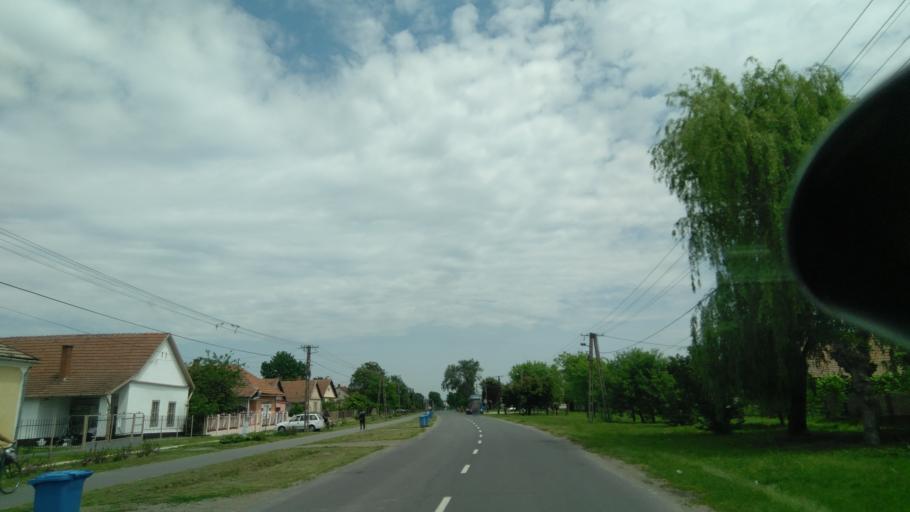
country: HU
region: Hajdu-Bihar
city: Komadi
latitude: 47.0098
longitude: 21.5019
